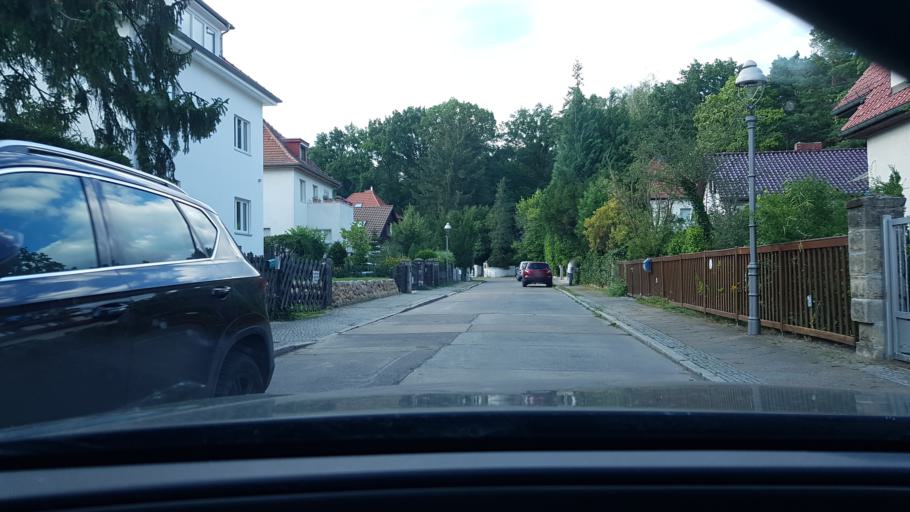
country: DE
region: Berlin
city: Frohnau
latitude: 52.6119
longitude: 13.2914
